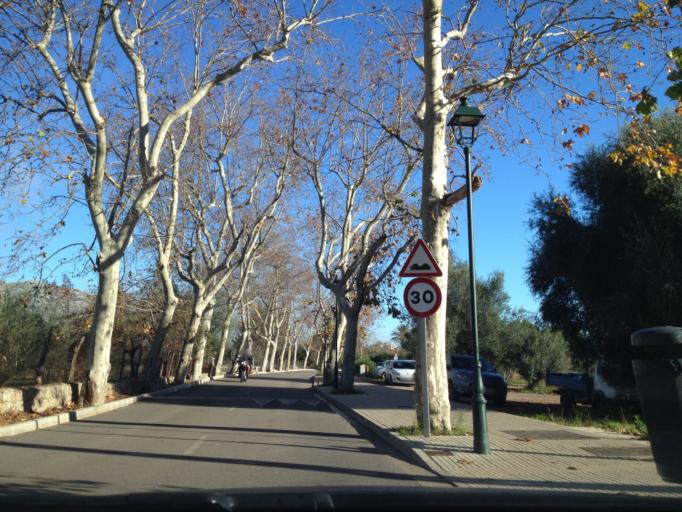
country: ES
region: Balearic Islands
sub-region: Illes Balears
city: Pollenca
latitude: 39.8826
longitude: 3.0195
